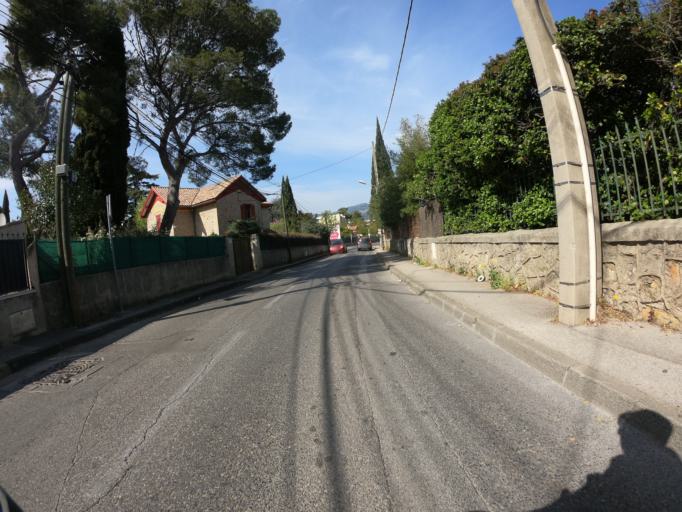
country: FR
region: Provence-Alpes-Cote d'Azur
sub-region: Departement du Var
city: La Valette-du-Var
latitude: 43.1125
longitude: 5.9801
